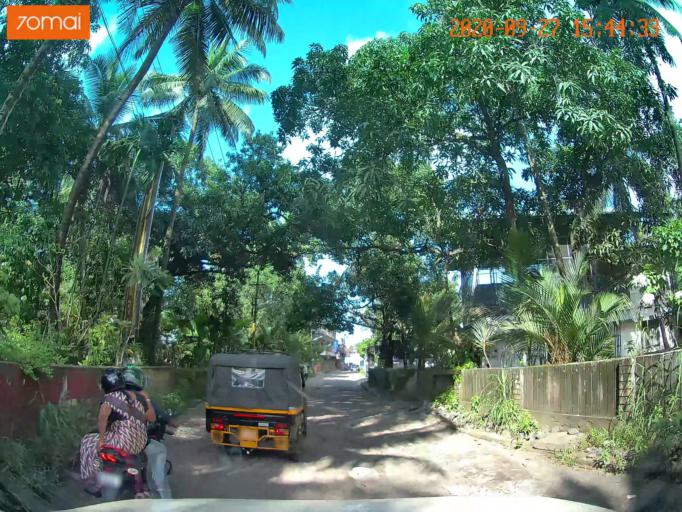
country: IN
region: Kerala
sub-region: Thrissur District
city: Thanniyam
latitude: 10.4766
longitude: 76.1131
